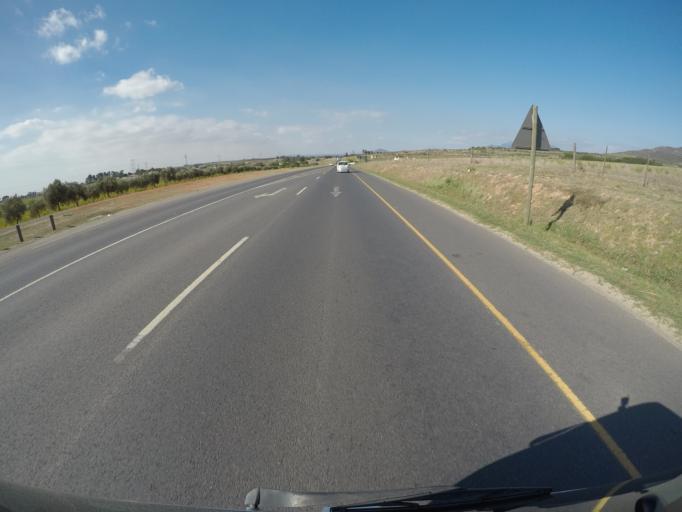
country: ZA
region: Western Cape
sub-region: City of Cape Town
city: Kraaifontein
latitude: -33.8923
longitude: 18.7393
